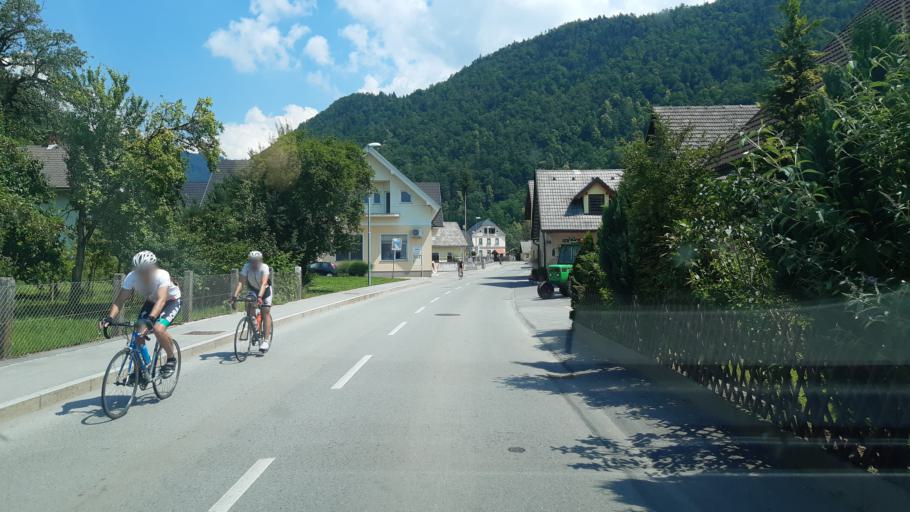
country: SI
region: Cerklje na Gorenjskem
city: Cerklje na Gorenjskem
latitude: 46.2612
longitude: 14.4923
